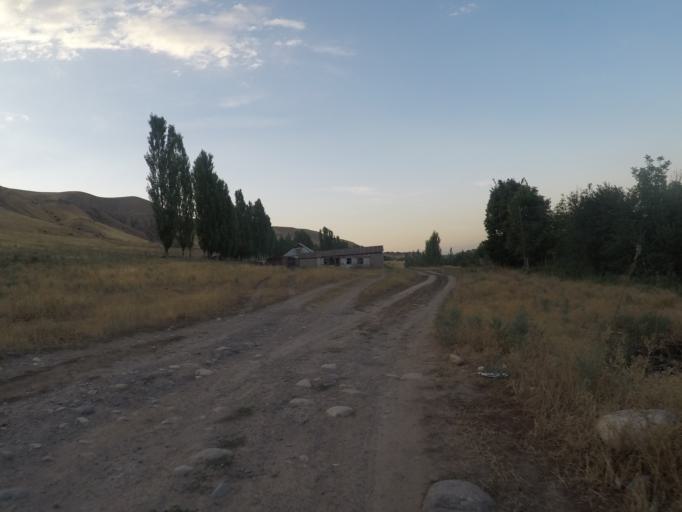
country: KG
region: Chuy
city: Bishkek
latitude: 42.7717
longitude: 74.6396
